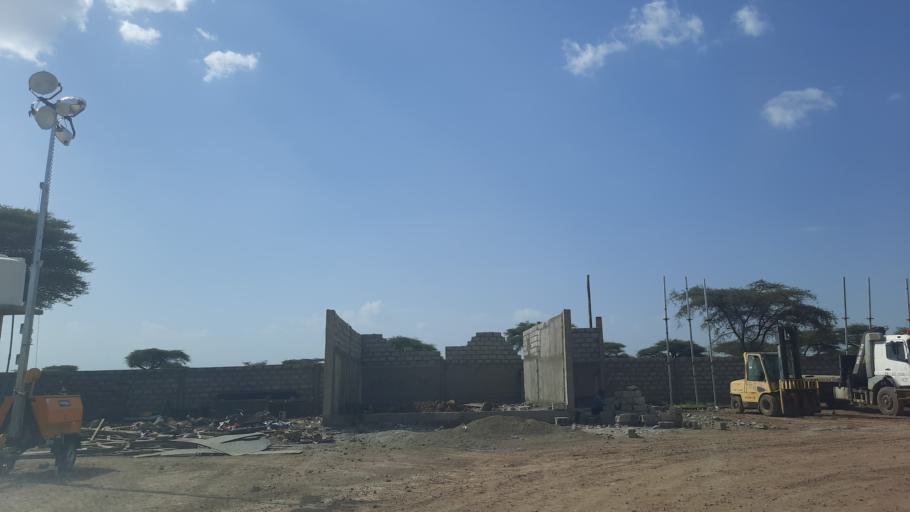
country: ET
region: Oromiya
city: Ziway
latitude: 7.7033
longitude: 38.6527
